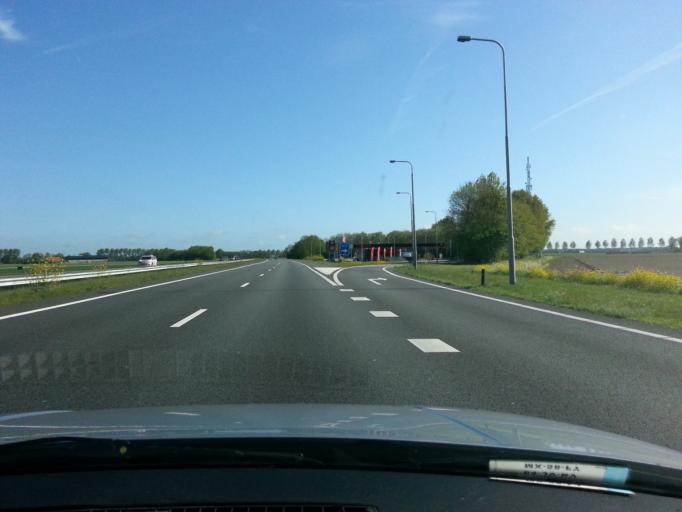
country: NL
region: Flevoland
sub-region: Gemeente Urk
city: Urk
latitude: 52.6243
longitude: 5.6641
